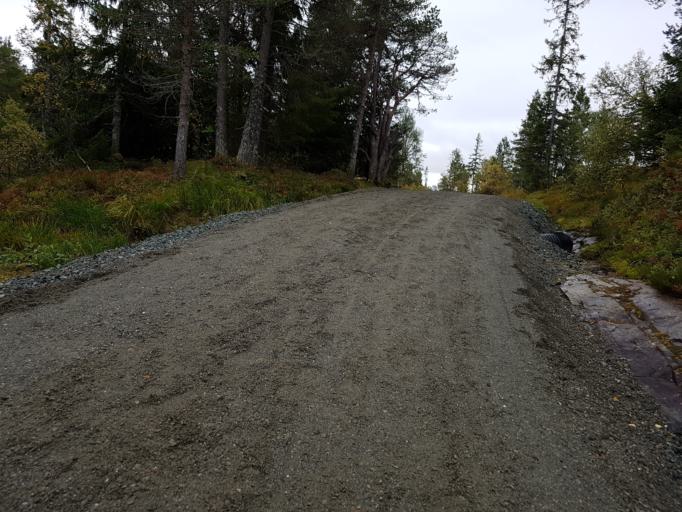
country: NO
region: Sor-Trondelag
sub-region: Melhus
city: Melhus
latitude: 63.4159
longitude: 10.2292
